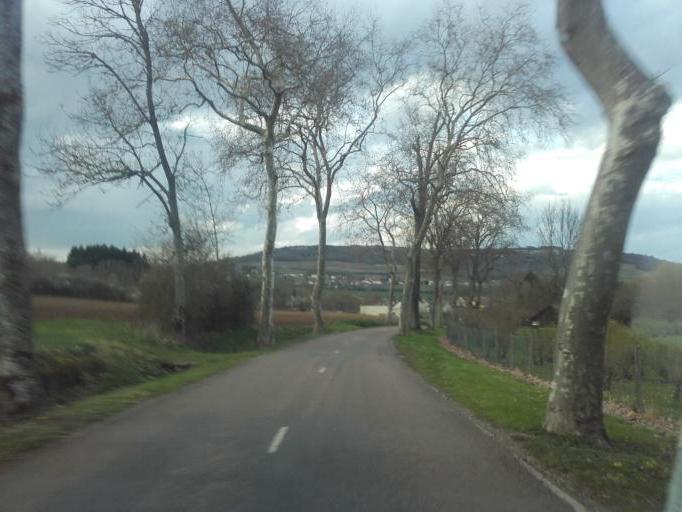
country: FR
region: Bourgogne
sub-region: Departement de la Cote-d'Or
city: Nolay
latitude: 46.9458
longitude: 4.6226
